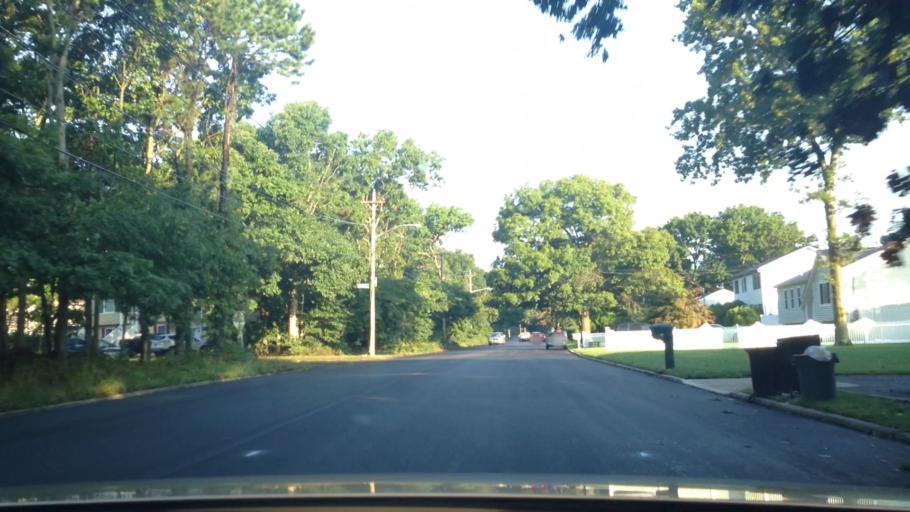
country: US
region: New York
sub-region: Suffolk County
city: Centereach
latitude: 40.8508
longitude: -73.0684
